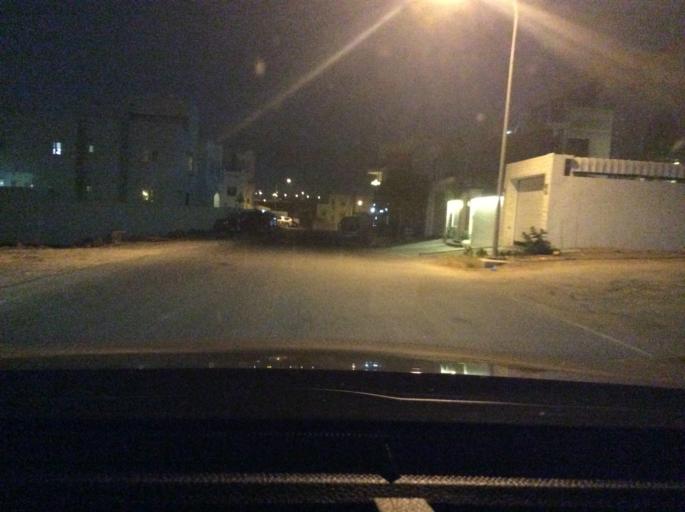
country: OM
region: Muhafazat Masqat
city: Bawshar
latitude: 23.5639
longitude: 58.3824
